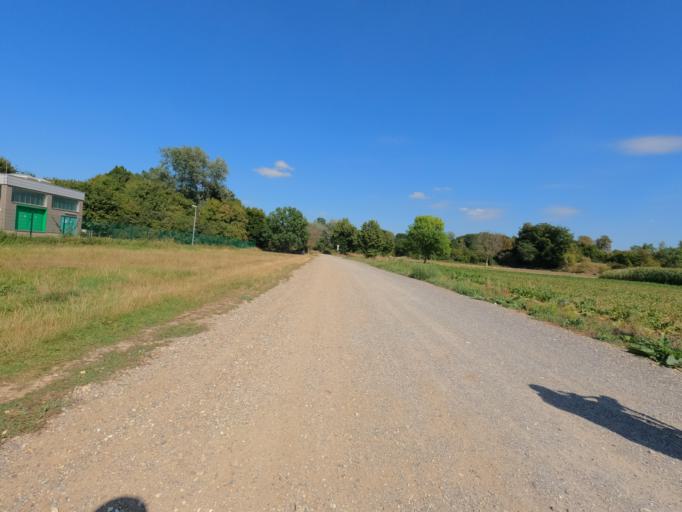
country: DE
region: North Rhine-Westphalia
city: Julich
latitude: 50.9300
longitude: 6.3432
